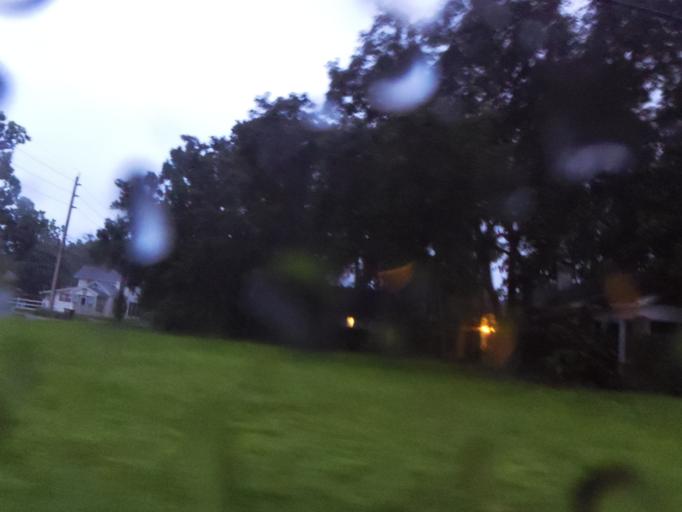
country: US
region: Florida
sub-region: Duval County
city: Jacksonville
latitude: 30.3137
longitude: -81.7266
